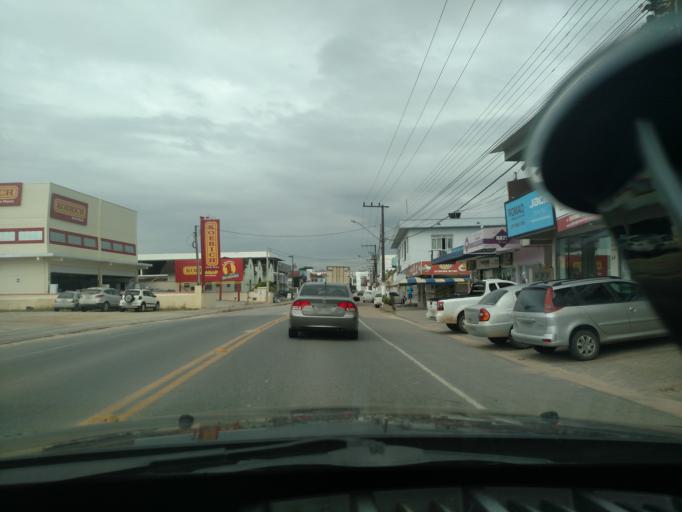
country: BR
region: Santa Catarina
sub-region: Gaspar
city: Gaspar
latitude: -26.9012
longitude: -48.8285
